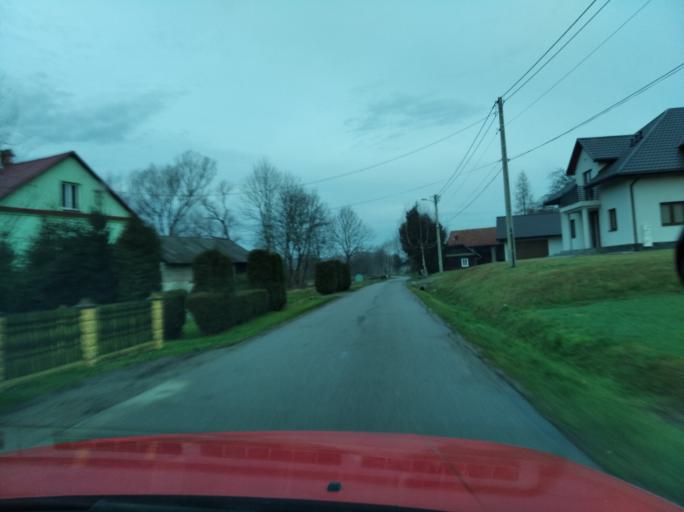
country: PL
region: Subcarpathian Voivodeship
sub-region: Powiat strzyzowski
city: Strzyzow
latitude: 49.8501
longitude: 21.8111
